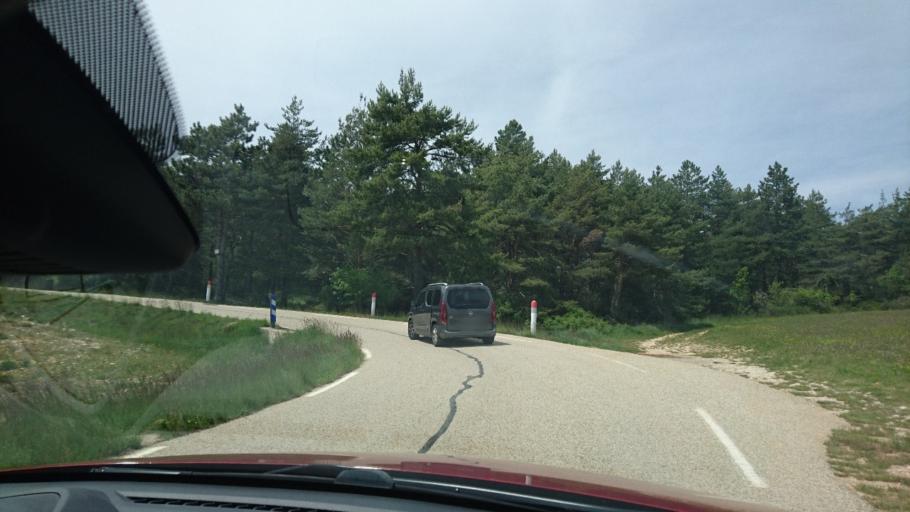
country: FR
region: Provence-Alpes-Cote d'Azur
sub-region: Departement du Vaucluse
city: Sault
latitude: 44.1176
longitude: 5.3864
